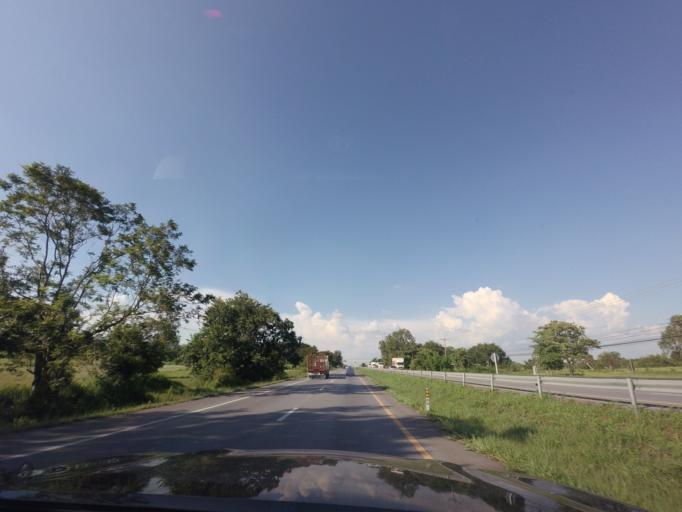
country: TH
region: Khon Kaen
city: Non Sila
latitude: 15.9741
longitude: 102.6938
